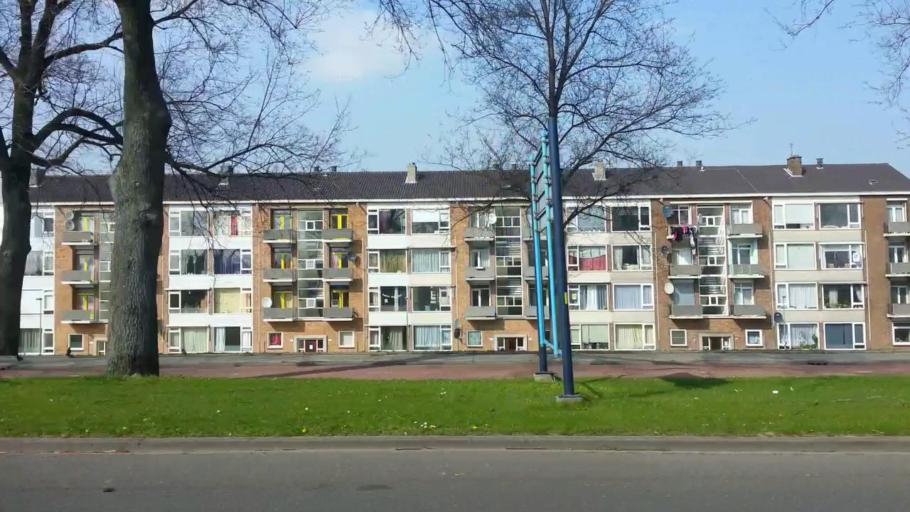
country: NL
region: South Holland
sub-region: Gemeente Schiedam
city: Schiedam
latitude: 51.9141
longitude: 4.4162
